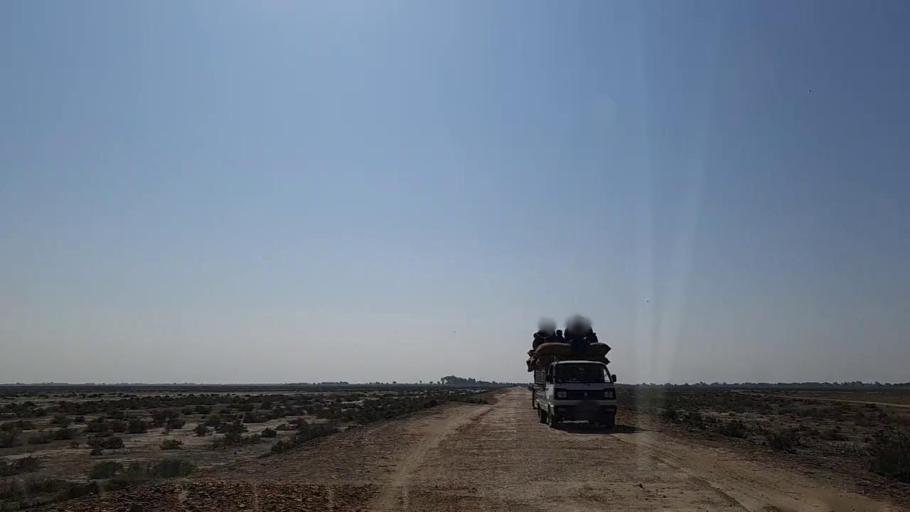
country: PK
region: Sindh
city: Chuhar Jamali
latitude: 24.5098
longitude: 68.0977
